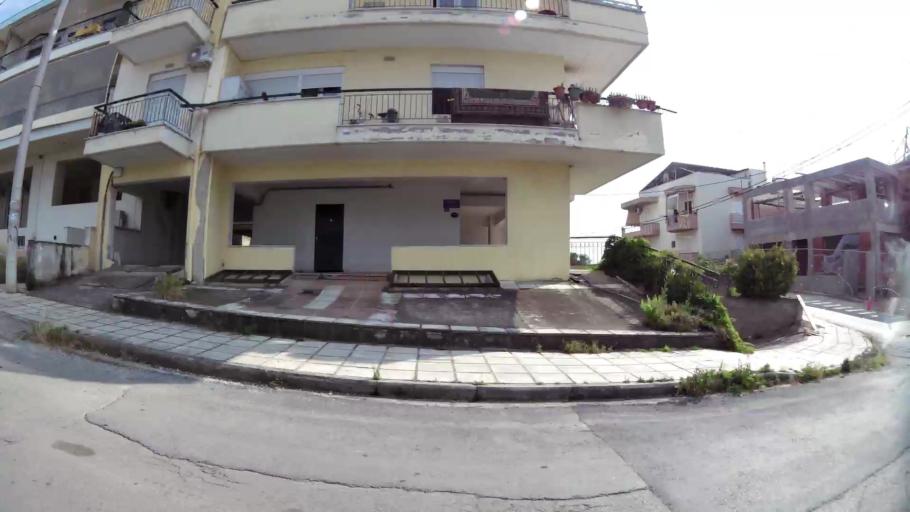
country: GR
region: Central Macedonia
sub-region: Nomos Thessalonikis
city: Polichni
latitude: 40.6610
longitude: 22.9633
